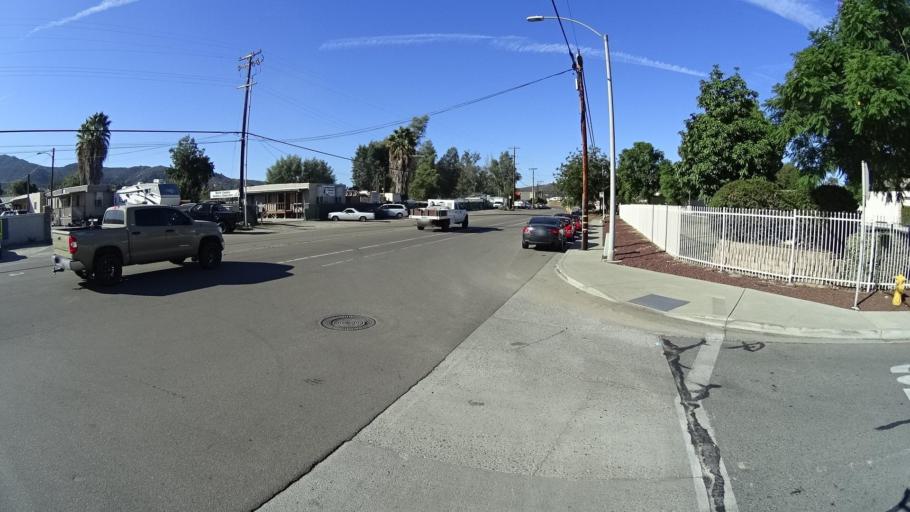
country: US
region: California
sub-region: San Diego County
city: Lakeside
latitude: 32.8412
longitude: -116.8909
